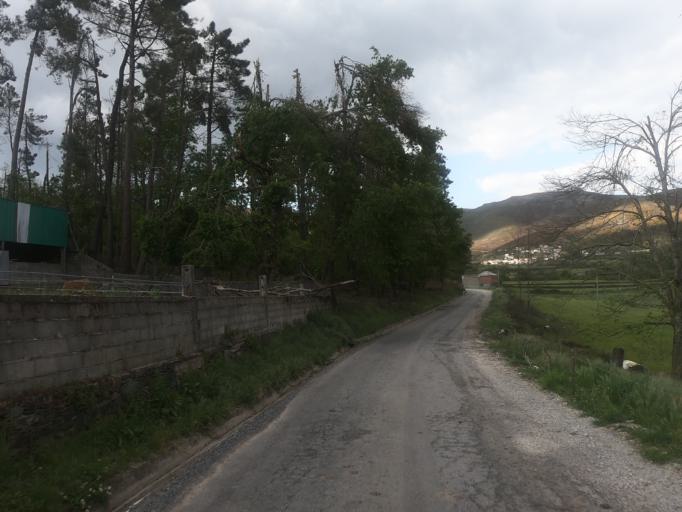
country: PT
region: Vila Real
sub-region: Santa Marta de Penaguiao
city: Santa Marta de Penaguiao
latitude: 41.3069
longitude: -7.8653
